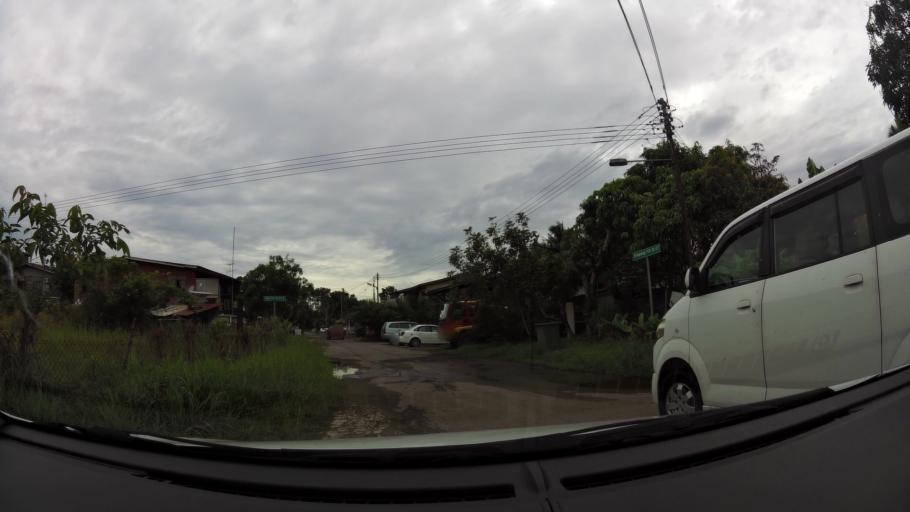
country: BN
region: Brunei and Muara
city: Bandar Seri Begawan
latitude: 4.8968
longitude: 114.9298
